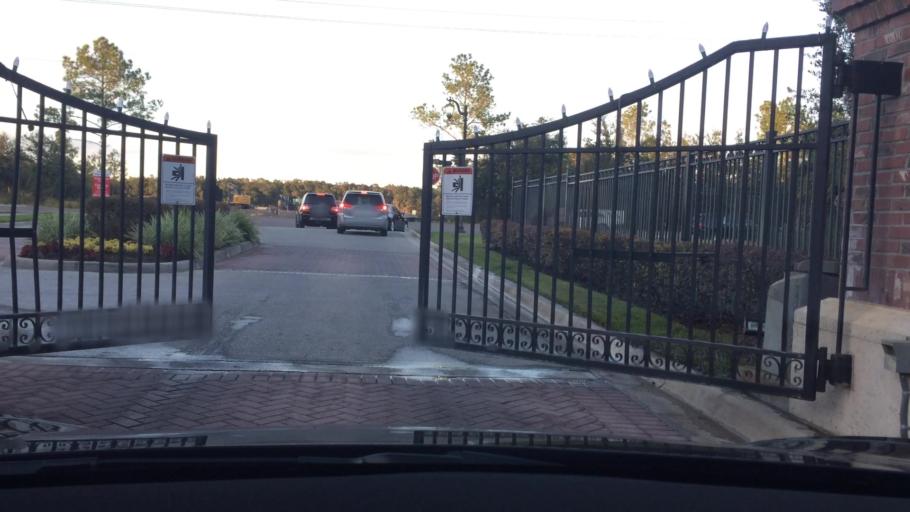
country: US
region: Florida
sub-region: Hillsborough County
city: Pebble Creek
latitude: 28.1706
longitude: -82.3823
